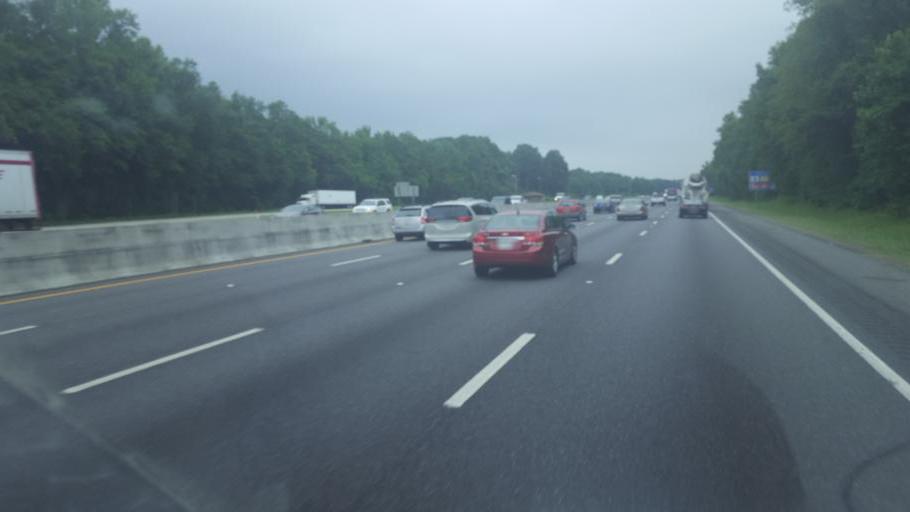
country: US
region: South Carolina
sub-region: York County
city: Fort Mill
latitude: 35.0136
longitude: -80.9698
